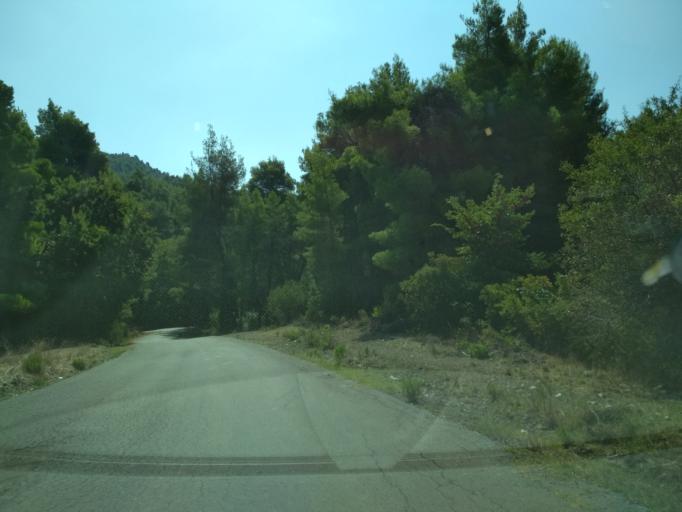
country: GR
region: Central Greece
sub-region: Nomos Evvoias
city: Roviai
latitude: 38.8270
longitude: 23.2663
